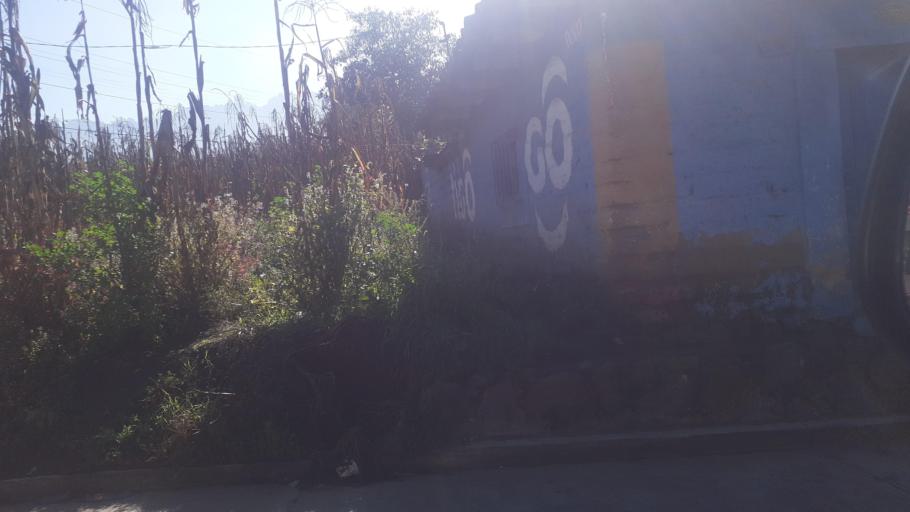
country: GT
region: Quetzaltenango
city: Cantel
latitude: 14.8181
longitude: -91.4488
